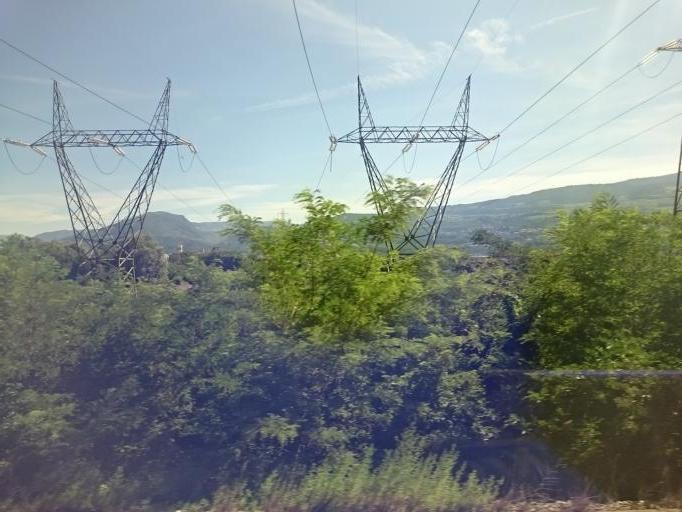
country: IT
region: Trentino-Alto Adige
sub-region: Provincia di Trento
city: Lavis
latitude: 46.1217
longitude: 11.0866
